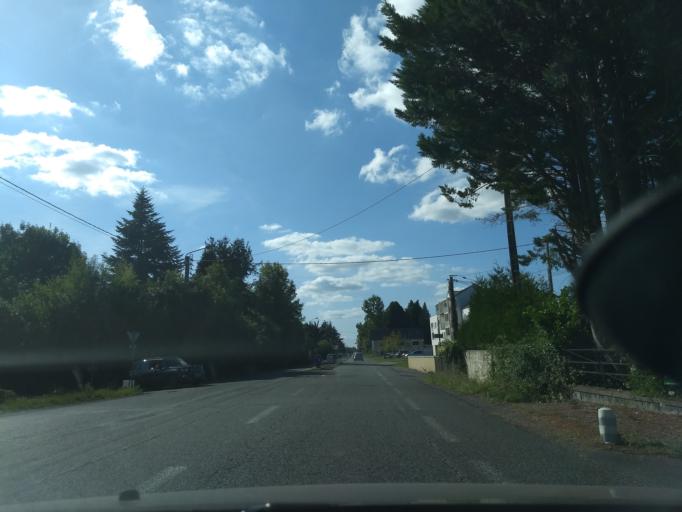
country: FR
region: Aquitaine
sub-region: Departement des Pyrenees-Atlantiques
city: Idron
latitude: 43.3010
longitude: -0.3132
